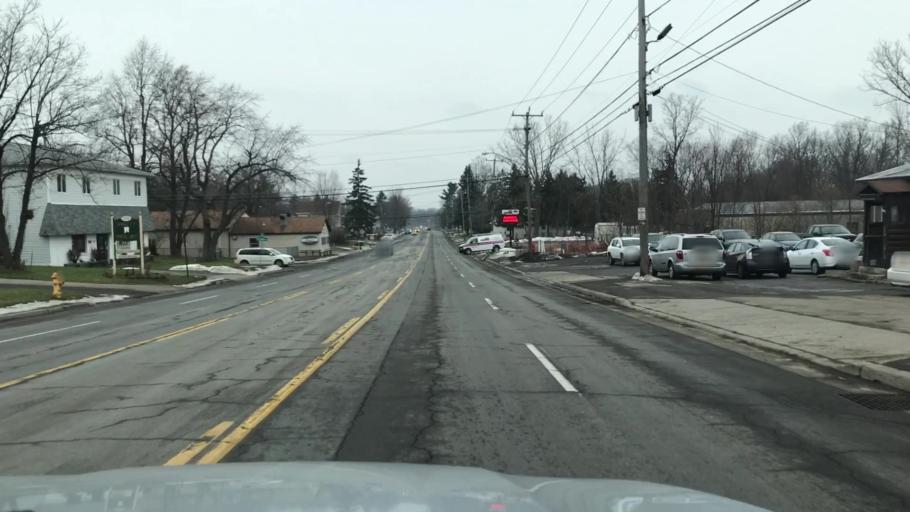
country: US
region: New York
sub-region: Erie County
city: Blasdell
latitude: 42.7822
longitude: -78.7901
